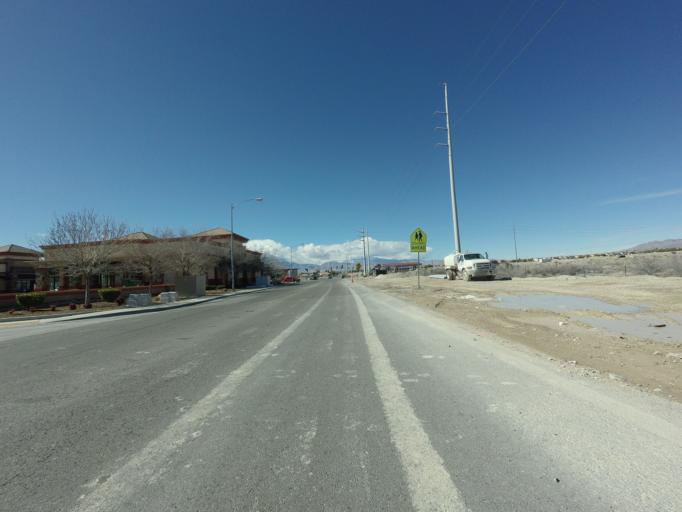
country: US
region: Nevada
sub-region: Clark County
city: Nellis Air Force Base
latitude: 36.2690
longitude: -115.1149
